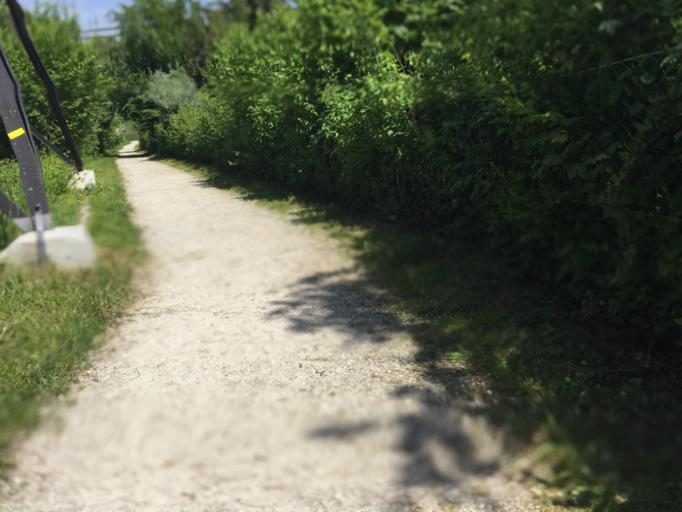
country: CH
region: Bern
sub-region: Bern-Mittelland District
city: Zollikofen
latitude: 46.9731
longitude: 7.4657
